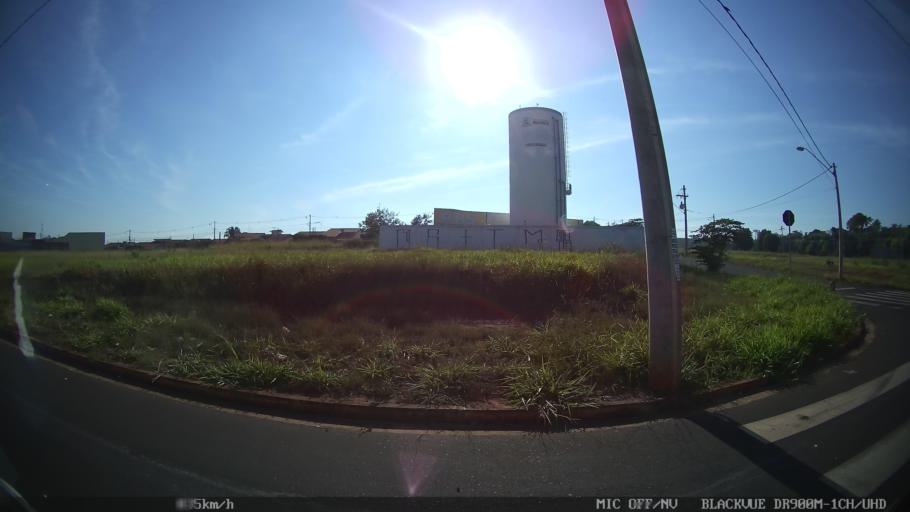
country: BR
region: Sao Paulo
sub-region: Sao Jose Do Rio Preto
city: Sao Jose do Rio Preto
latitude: -20.7669
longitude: -49.3564
